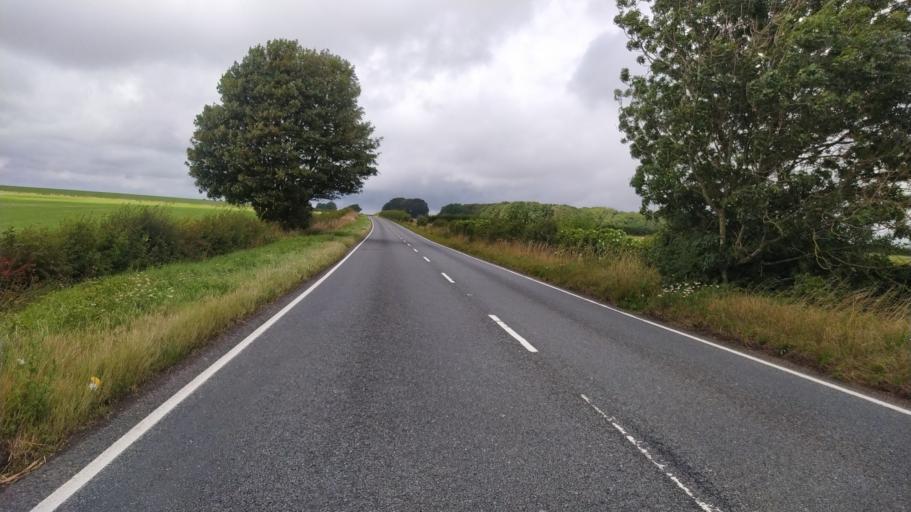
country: GB
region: England
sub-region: Hampshire
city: Kings Worthy
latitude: 51.0426
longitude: -1.2304
